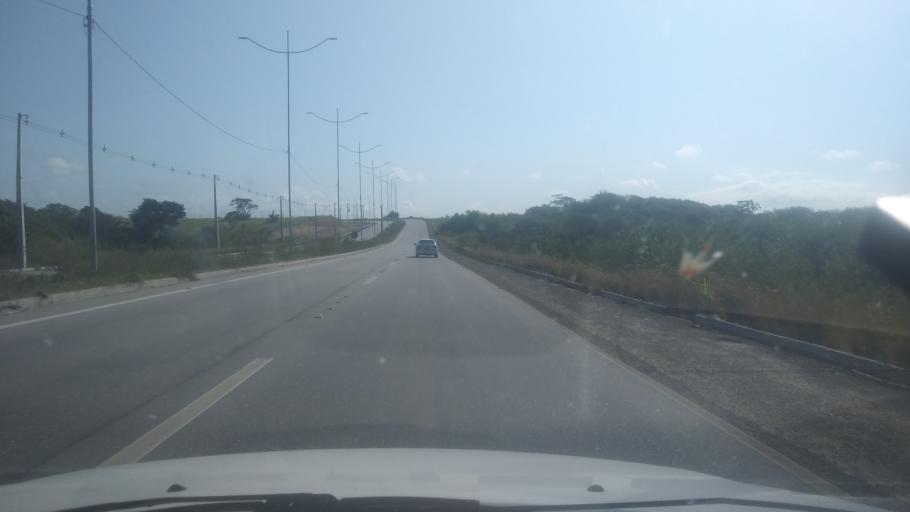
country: BR
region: Rio Grande do Norte
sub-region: Macaiba
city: Macaiba
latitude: -5.8340
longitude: -35.3724
